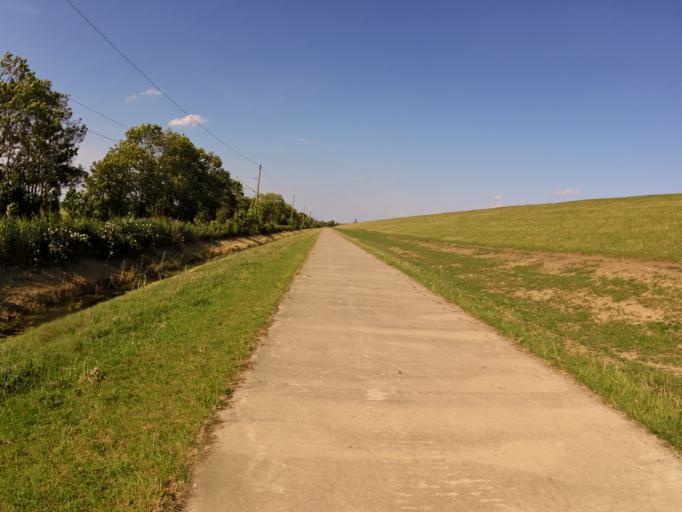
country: DE
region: Lower Saxony
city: Nordenham
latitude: 53.4556
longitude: 8.4748
